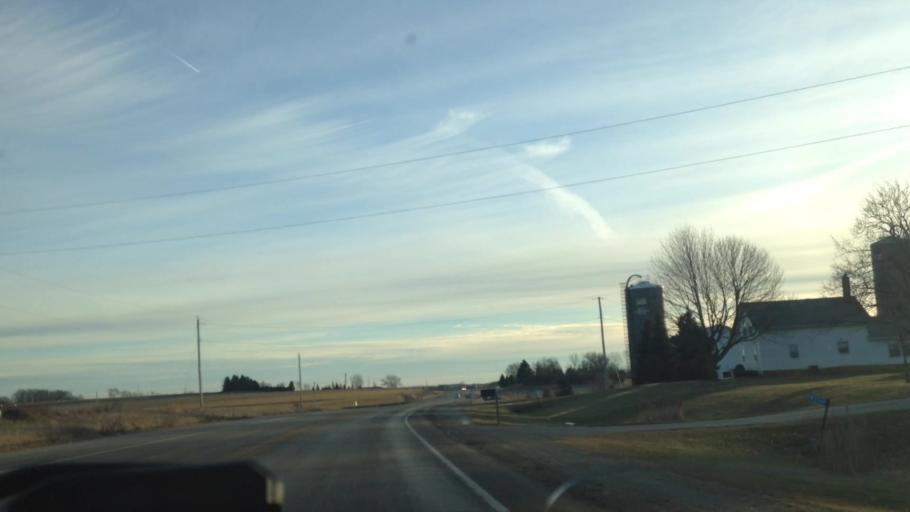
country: US
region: Wisconsin
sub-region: Dodge County
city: Mayville
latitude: 43.5152
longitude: -88.5252
